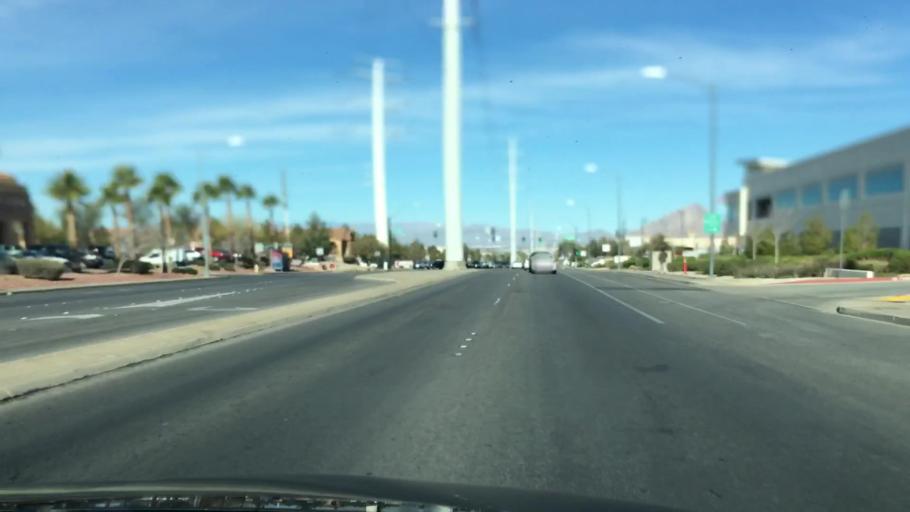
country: US
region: Nevada
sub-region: Clark County
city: Henderson
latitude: 36.0403
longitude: -115.0293
